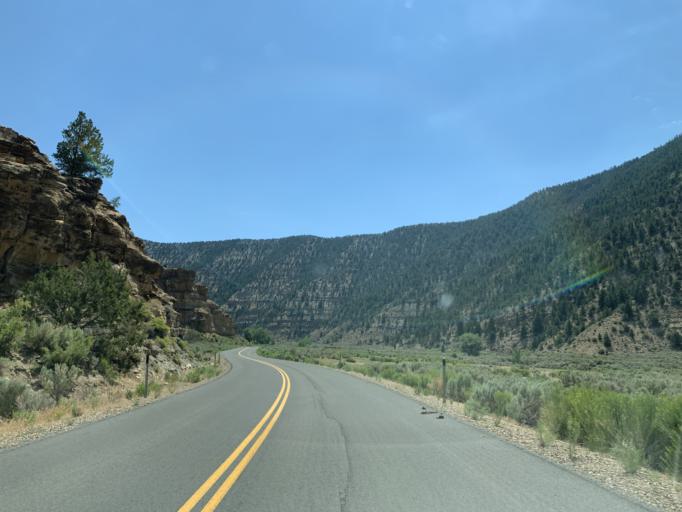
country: US
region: Utah
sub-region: Carbon County
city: East Carbon City
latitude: 39.7861
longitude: -110.4089
